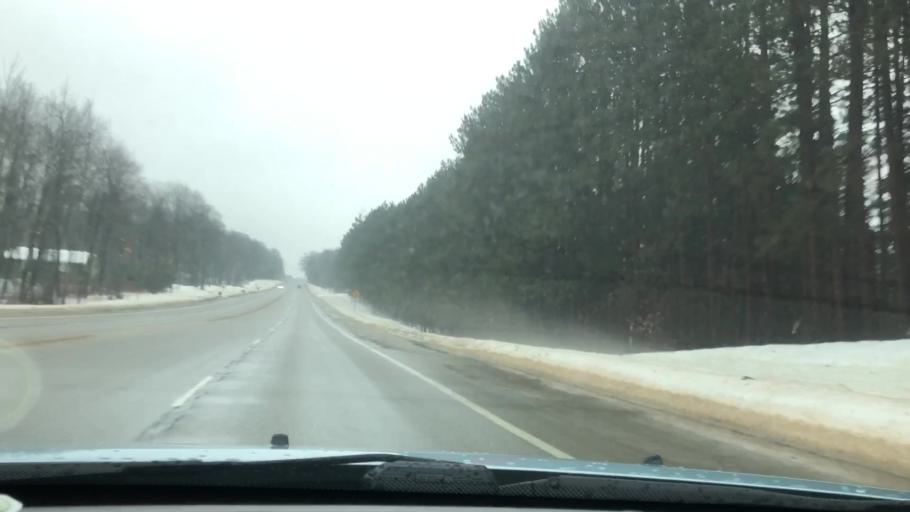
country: US
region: Michigan
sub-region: Otsego County
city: Gaylord
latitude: 45.0419
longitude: -84.7759
